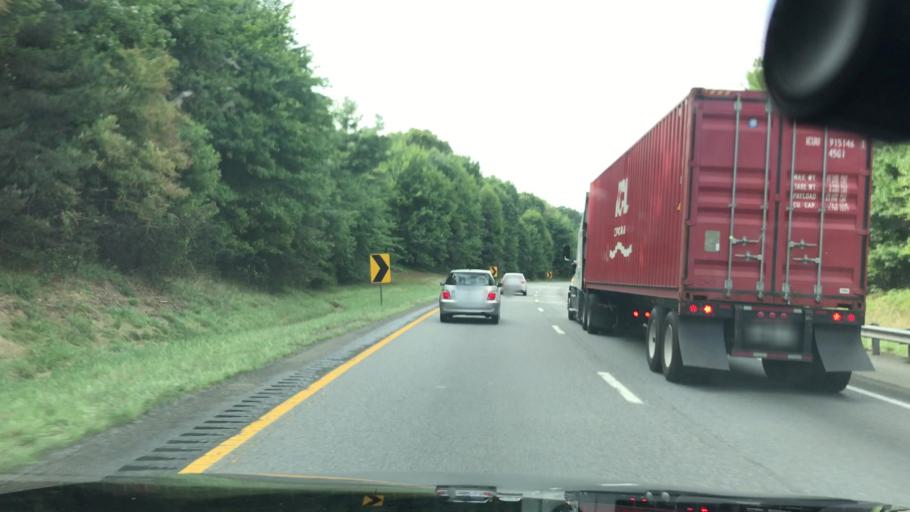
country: US
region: Virginia
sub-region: Carroll County
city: Woodlawn
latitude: 36.8082
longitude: -80.8536
